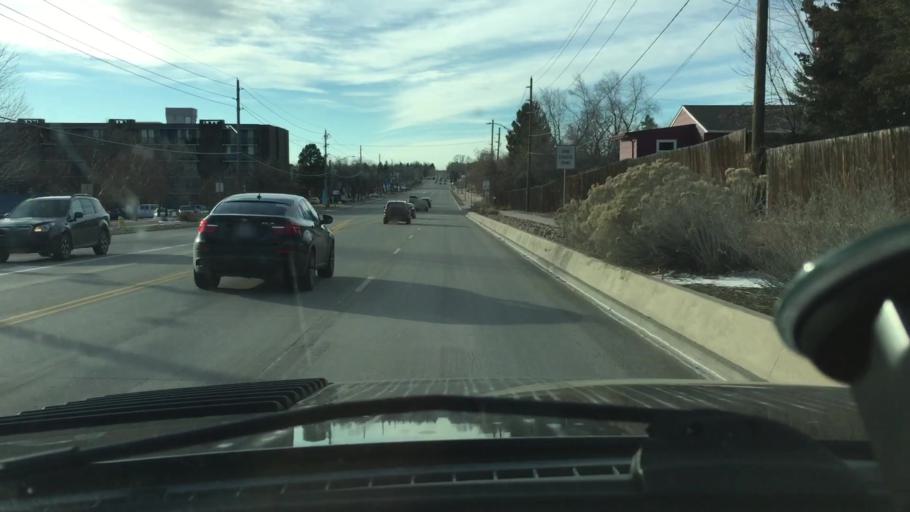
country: US
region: Colorado
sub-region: Adams County
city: Northglenn
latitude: 39.8927
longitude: -104.9968
